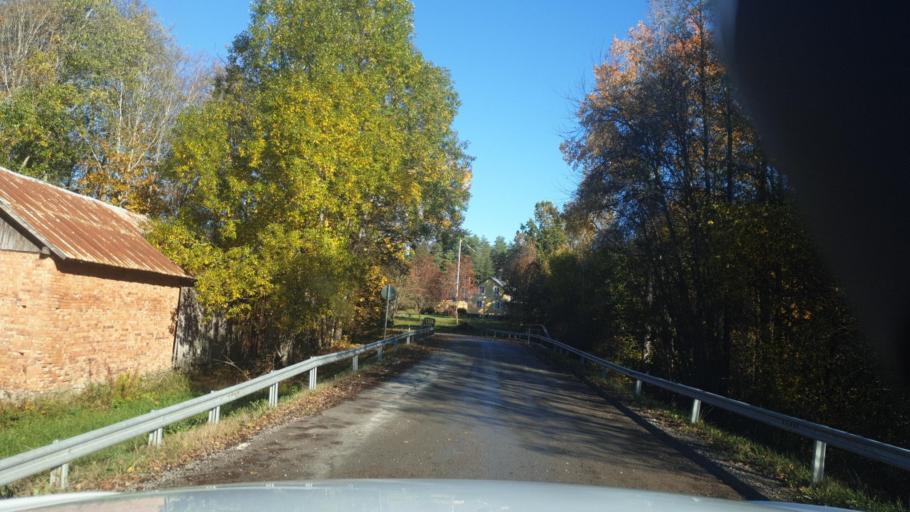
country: SE
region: Vaermland
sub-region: Arvika Kommun
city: Arvika
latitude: 59.5295
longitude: 12.7412
